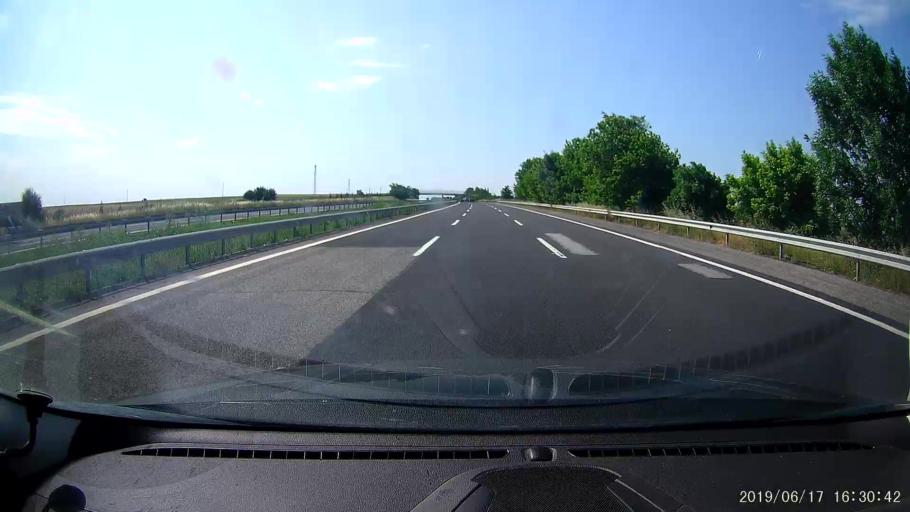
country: TR
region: Tekirdag
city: Beyazkoy
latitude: 41.3515
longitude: 27.6477
